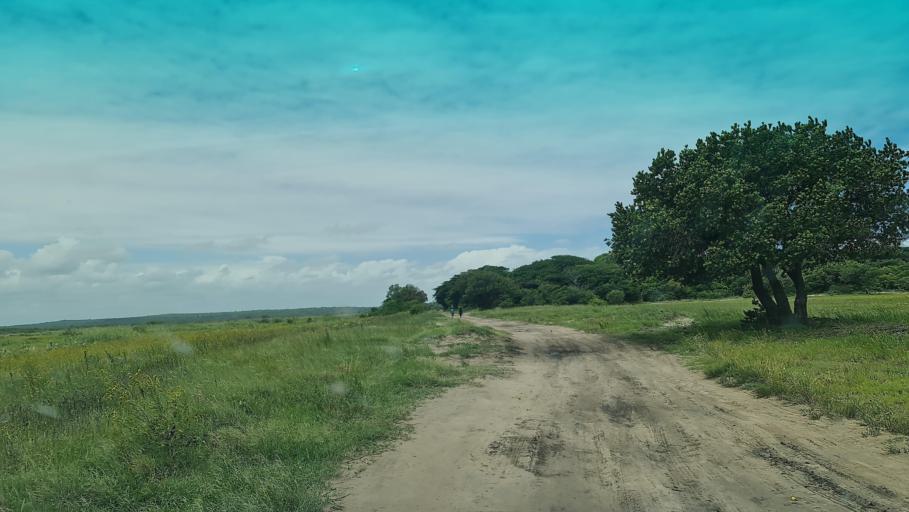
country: MZ
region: Maputo
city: Manhica
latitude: -25.5285
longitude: 32.8502
